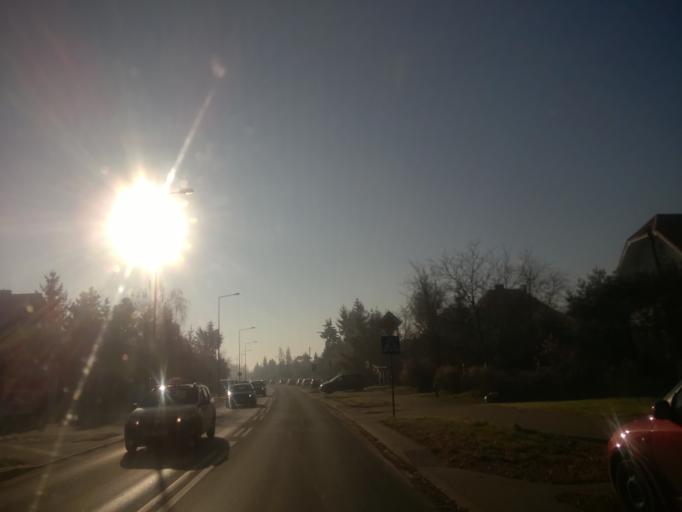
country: PL
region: Lower Silesian Voivodeship
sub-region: Powiat wroclawski
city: Wroclaw
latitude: 51.0683
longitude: 17.0320
